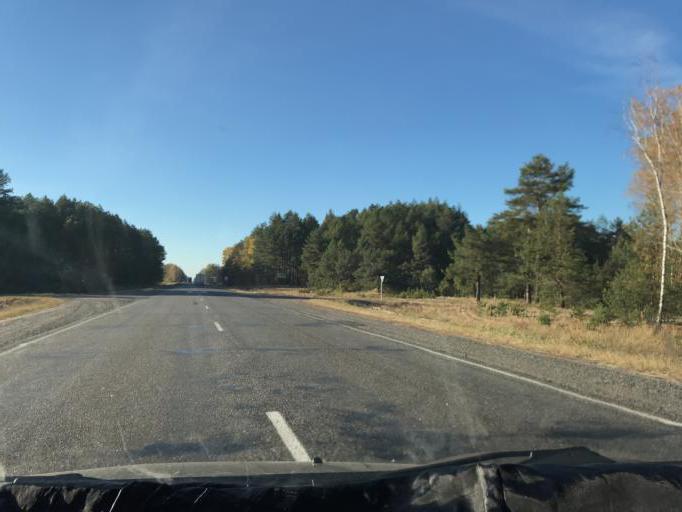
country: BY
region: Gomel
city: Mazyr
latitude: 52.1985
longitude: 29.0942
